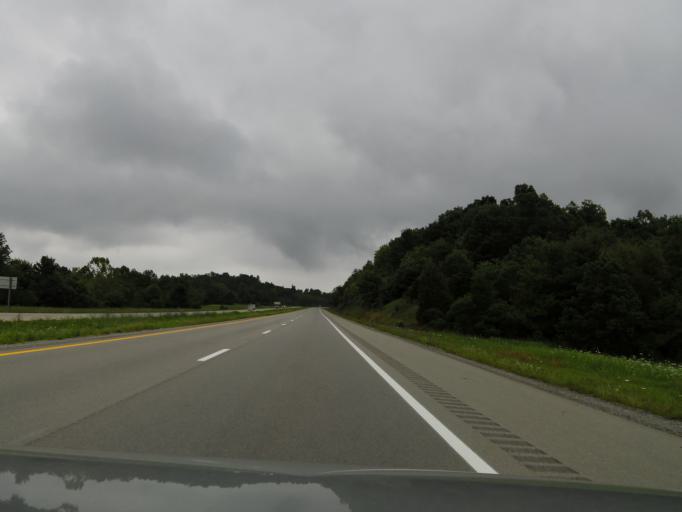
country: US
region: Kentucky
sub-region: Ohio County
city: Oak Grove
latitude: 37.4050
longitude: -86.5521
